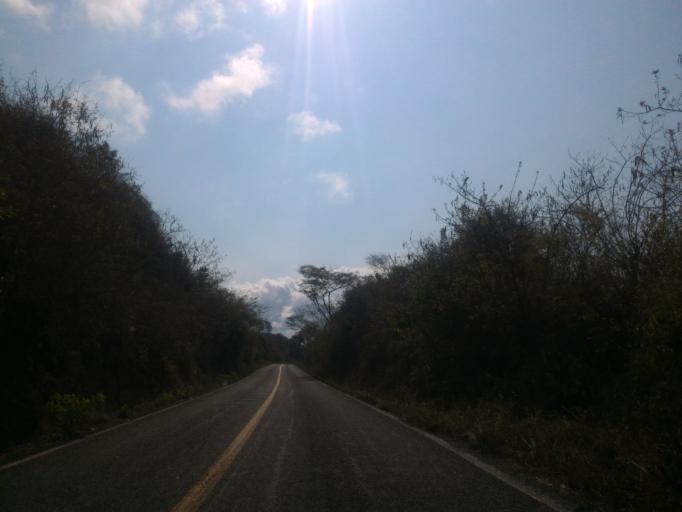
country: MX
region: Michoacan
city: Coahuayana Viejo
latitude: 18.4815
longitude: -103.5668
